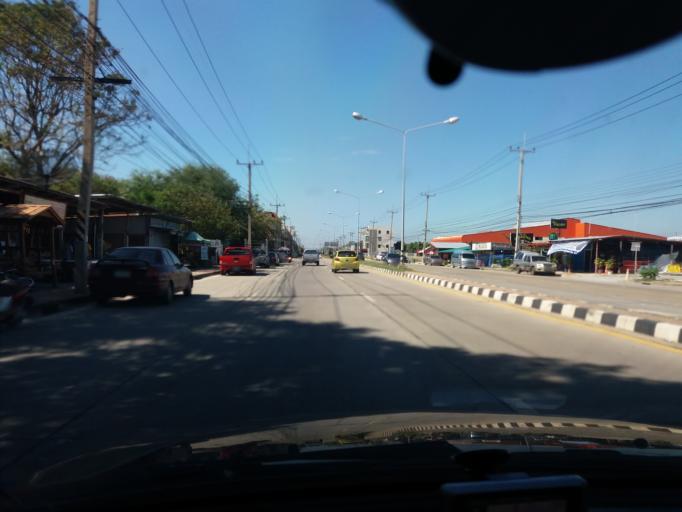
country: TH
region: Suphan Buri
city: Suphan Buri
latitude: 14.4629
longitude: 100.1426
